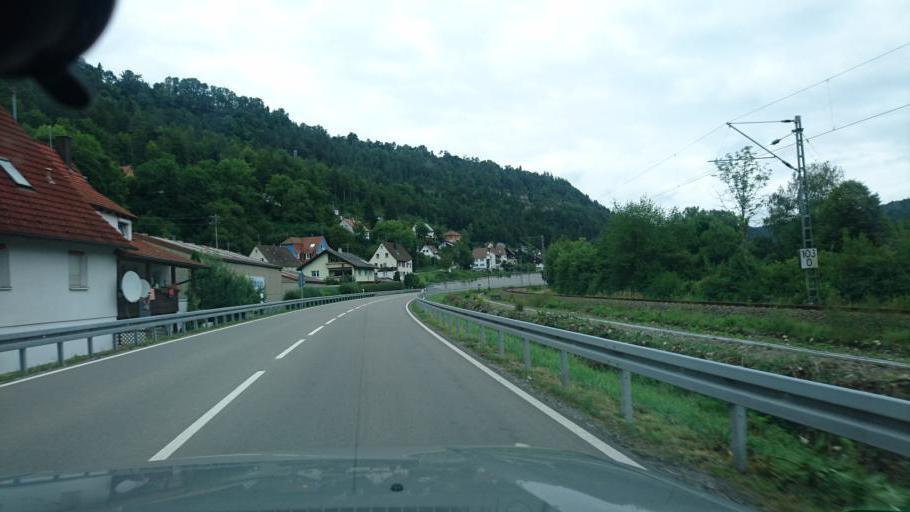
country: DE
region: Baden-Wuerttemberg
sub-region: Freiburg Region
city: Oberndorf
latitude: 48.3174
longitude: 8.5715
